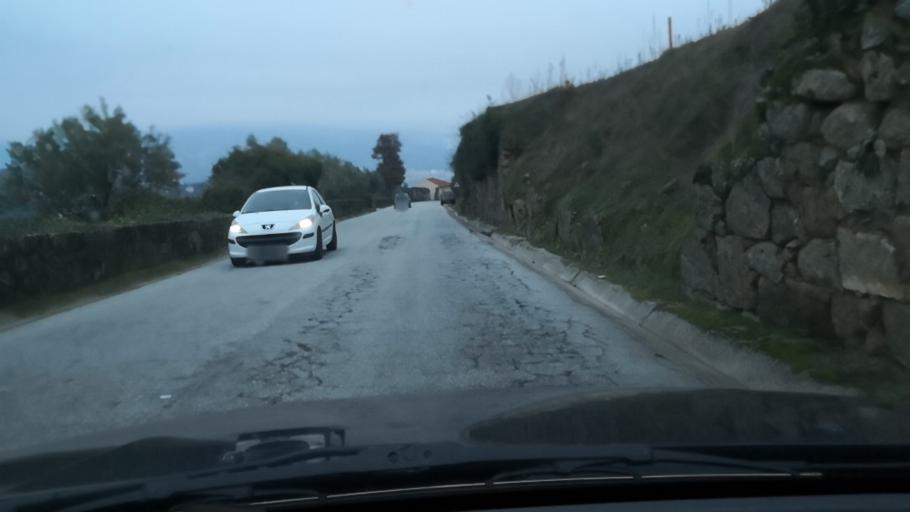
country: PT
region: Viseu
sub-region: Lamego
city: Lamego
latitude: 41.1147
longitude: -7.8036
